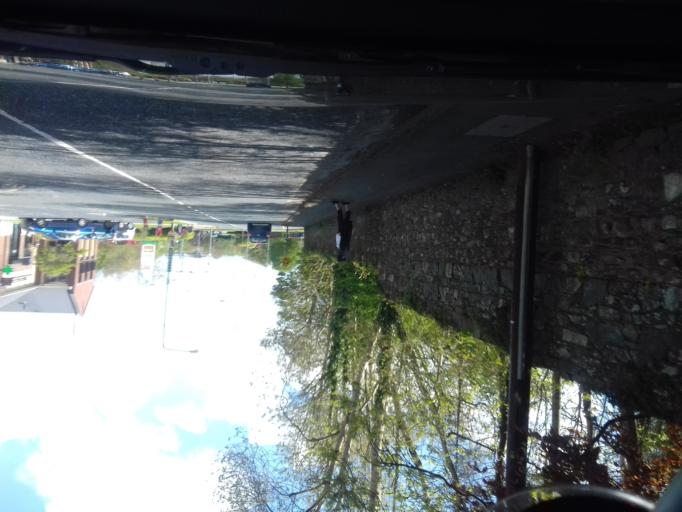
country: IE
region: Munster
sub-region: Waterford
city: Waterford
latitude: 52.2404
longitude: -7.0667
